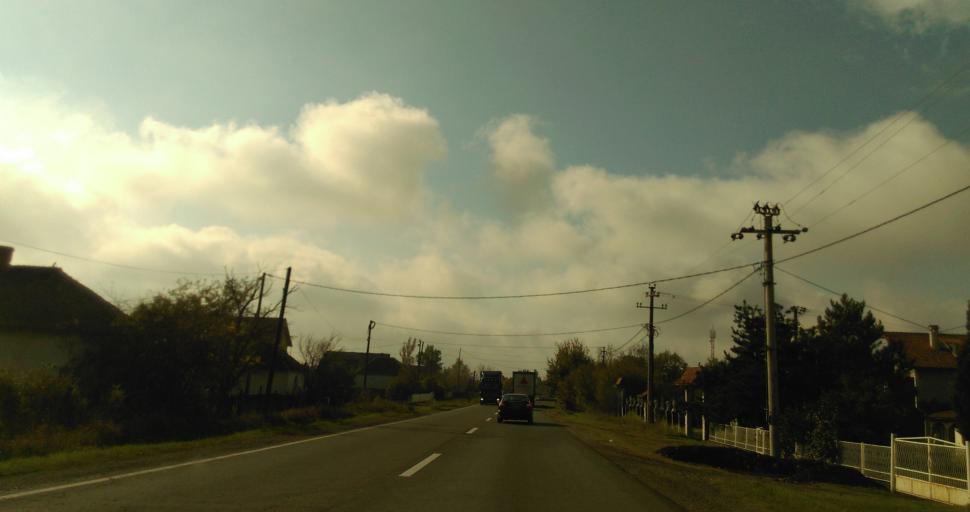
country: RS
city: Stepojevac
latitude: 44.5240
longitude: 20.2932
